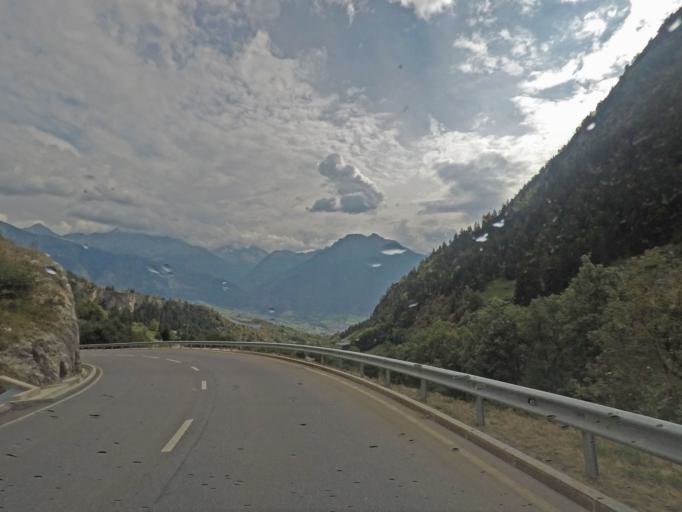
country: CH
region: Valais
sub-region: Brig District
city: Naters
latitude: 46.3525
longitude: 7.9794
